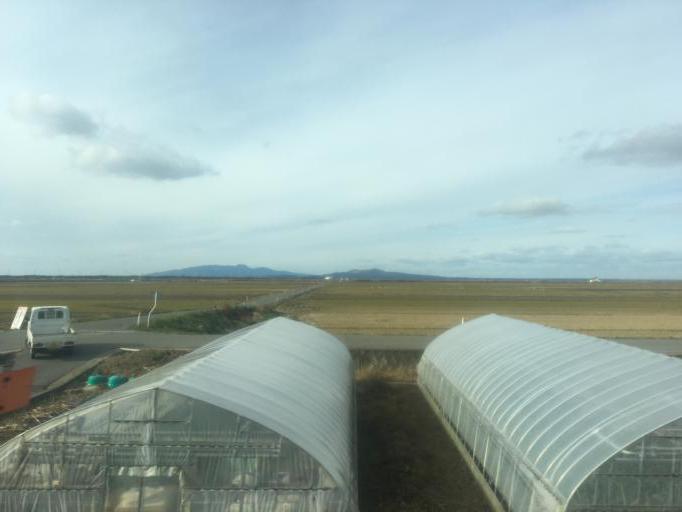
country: JP
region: Akita
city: Tenno
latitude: 39.8823
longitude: 140.0671
